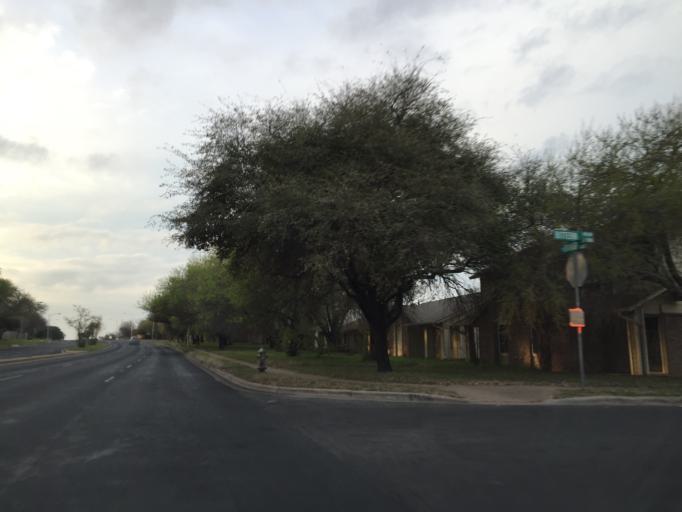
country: US
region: Texas
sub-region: Travis County
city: Wells Branch
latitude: 30.3894
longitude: -97.7014
